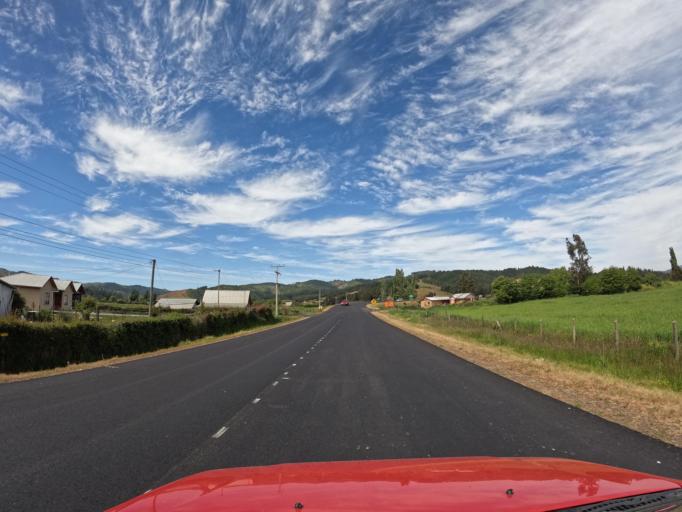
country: CL
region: Maule
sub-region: Provincia de Talca
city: Constitucion
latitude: -35.0766
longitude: -72.0265
